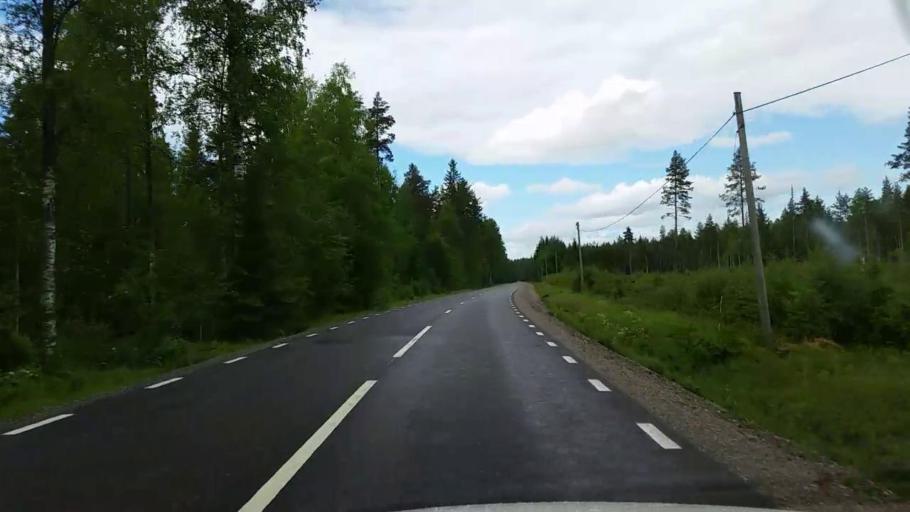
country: SE
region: Gaevleborg
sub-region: Sandvikens Kommun
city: Jarbo
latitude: 60.8532
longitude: 16.4436
